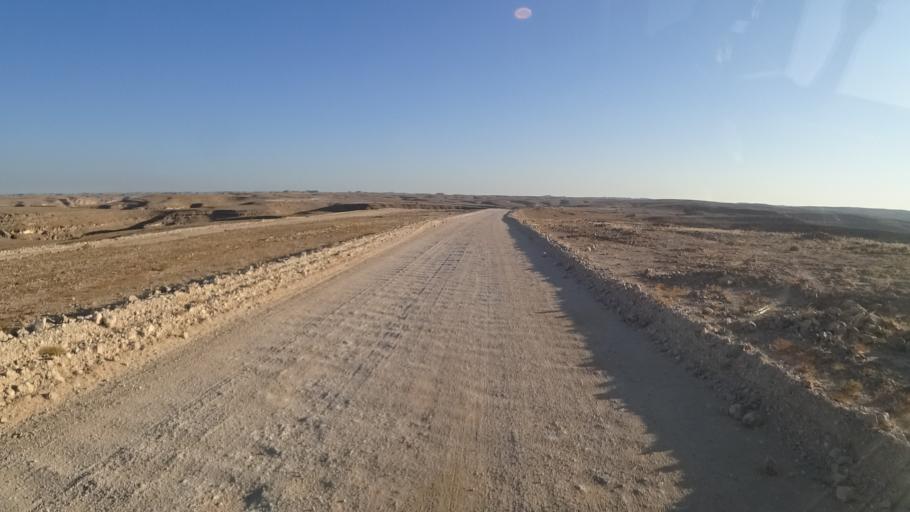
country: YE
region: Al Mahrah
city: Hawf
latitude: 17.1945
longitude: 53.3390
